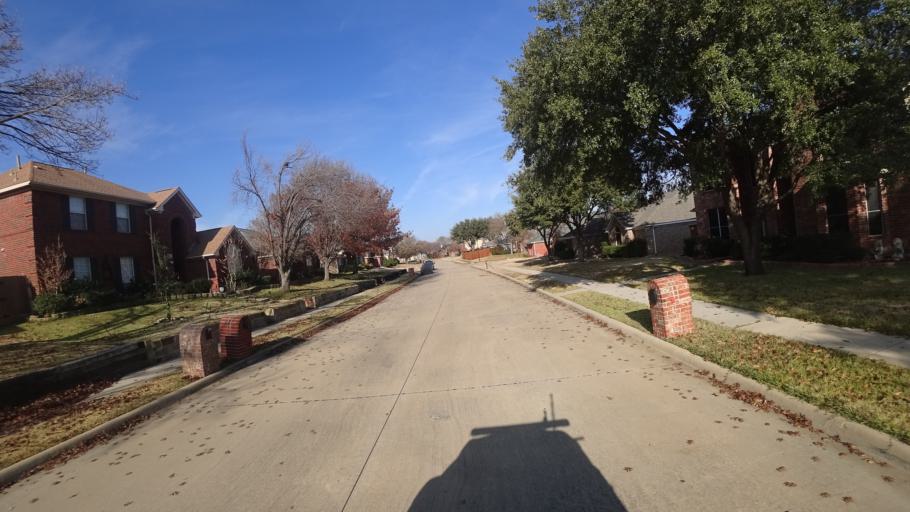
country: US
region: Texas
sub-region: Denton County
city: Lewisville
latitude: 33.0519
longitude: -97.0210
